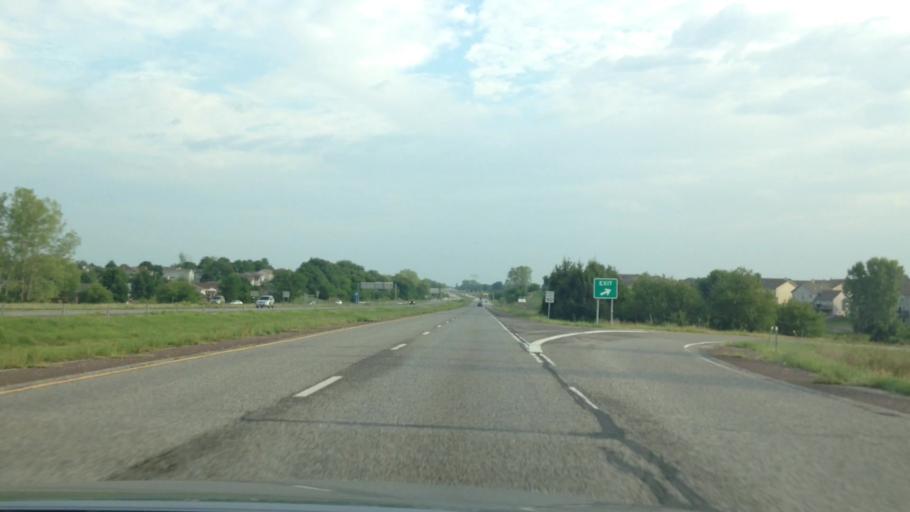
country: US
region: Missouri
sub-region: Clay County
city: Smithville
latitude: 39.3029
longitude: -94.5848
